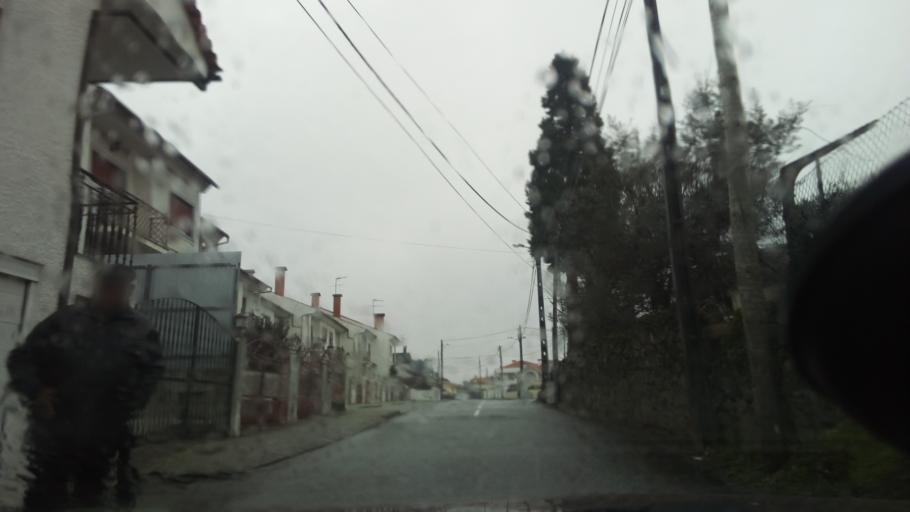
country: PT
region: Viseu
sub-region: Viseu
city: Rio de Loba
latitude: 40.6630
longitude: -7.8759
